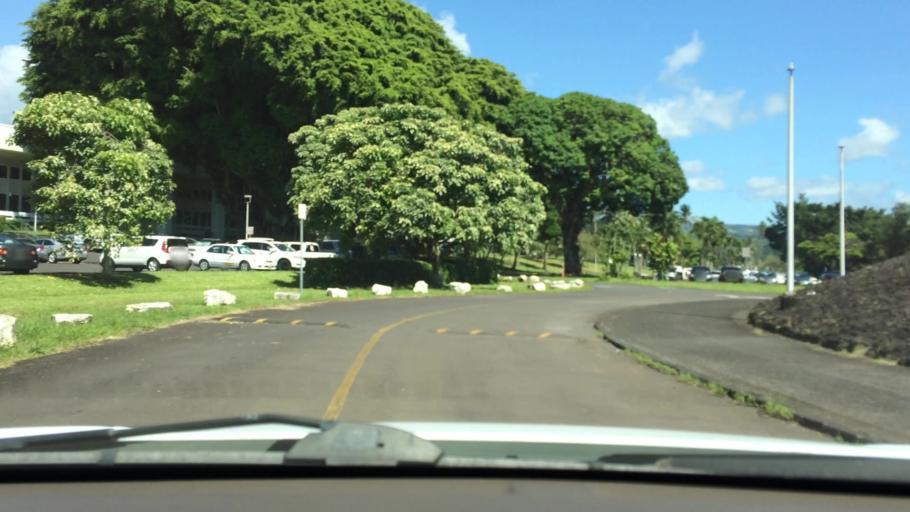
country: US
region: Hawaii
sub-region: Hawaii County
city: Hilo
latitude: 19.7191
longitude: -155.0760
